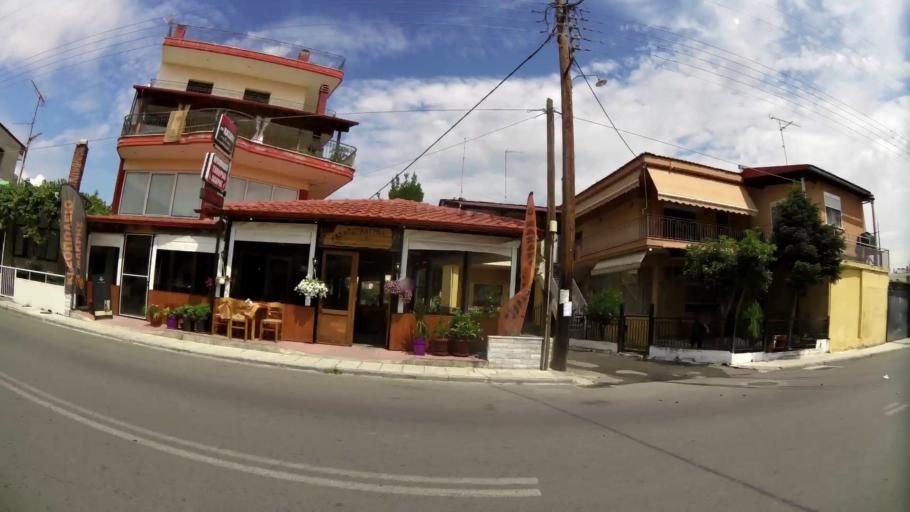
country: GR
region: Central Macedonia
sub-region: Nomos Pierias
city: Katerini
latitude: 40.2792
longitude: 22.4960
